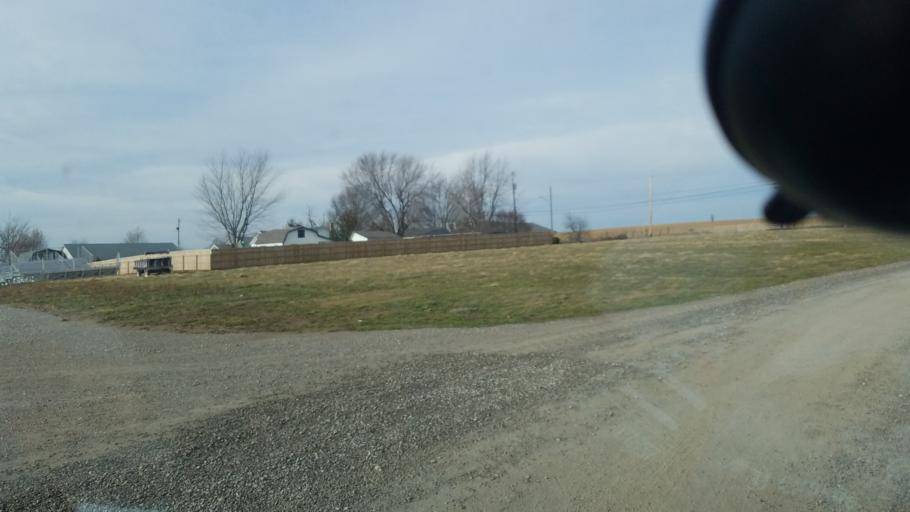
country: US
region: Ohio
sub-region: Wayne County
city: Apple Creek
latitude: 40.6232
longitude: -81.7900
